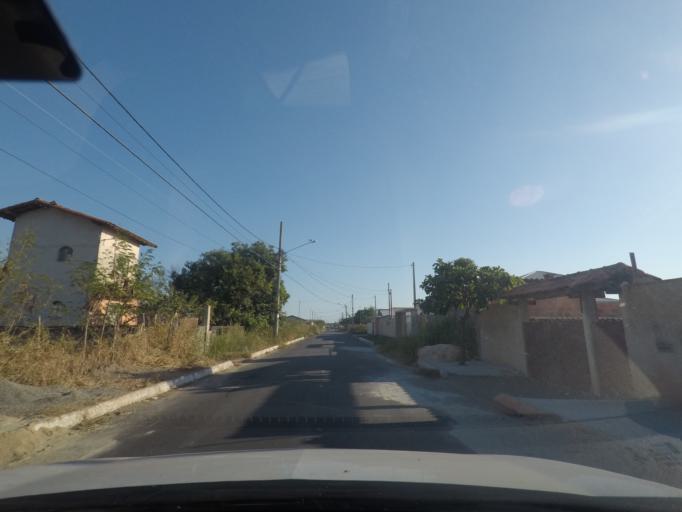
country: BR
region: Rio de Janeiro
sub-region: Marica
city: Marica
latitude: -22.9577
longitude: -42.9379
